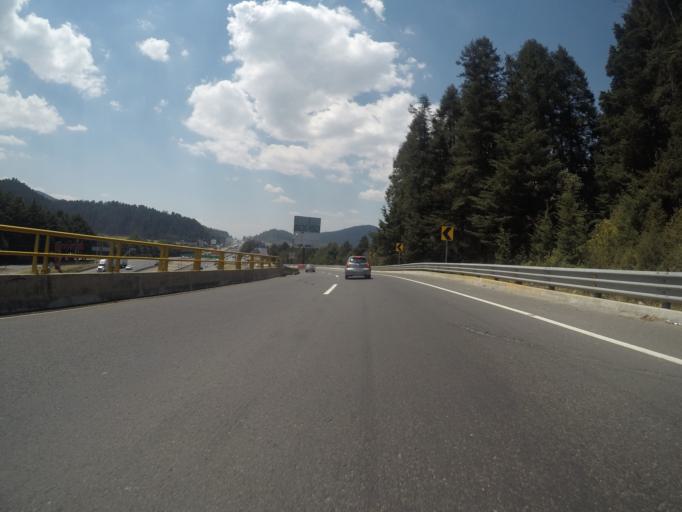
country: MX
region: Mexico
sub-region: Huixquilucan
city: El Palacio
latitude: 19.3014
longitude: -99.3760
